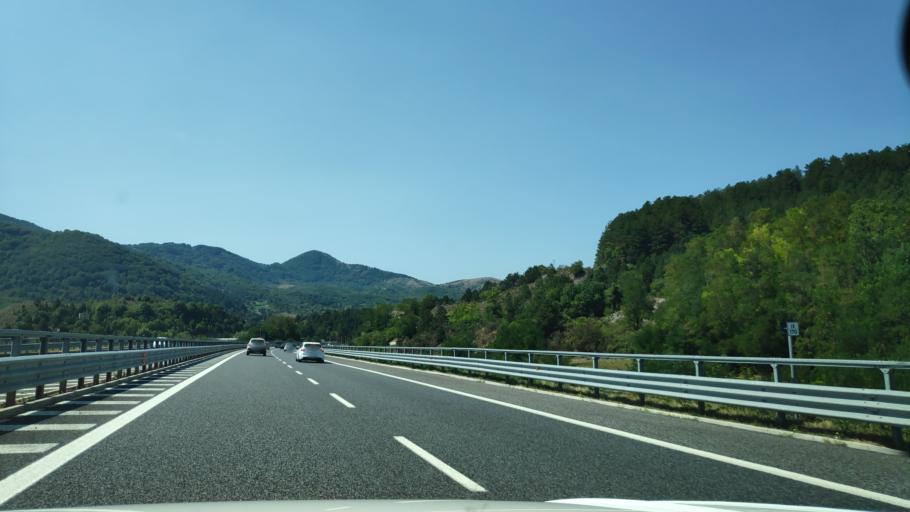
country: IT
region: Calabria
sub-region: Provincia di Cosenza
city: Mormanno
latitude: 39.8817
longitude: 16.0107
